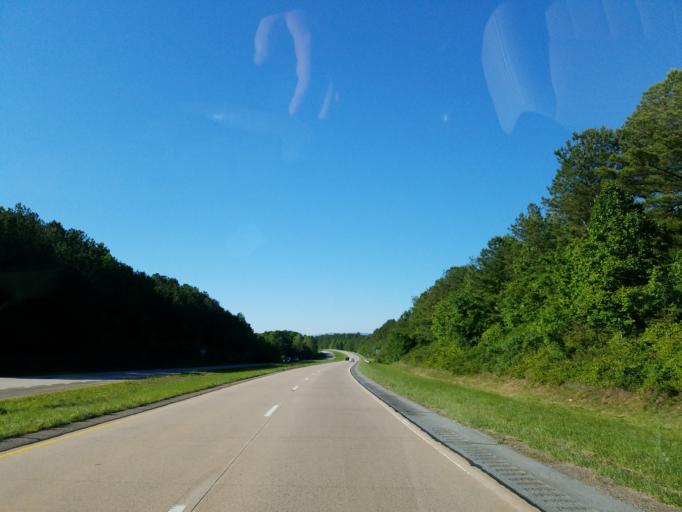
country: US
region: Georgia
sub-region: Pickens County
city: Jasper
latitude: 34.5535
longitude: -84.5217
